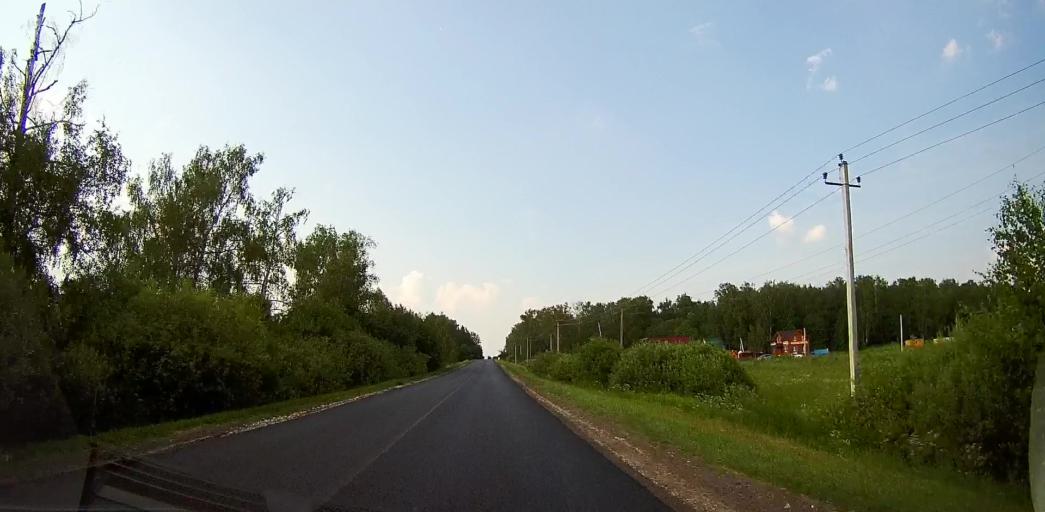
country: RU
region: Moskovskaya
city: Il'inskoye
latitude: 55.2314
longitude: 37.9226
